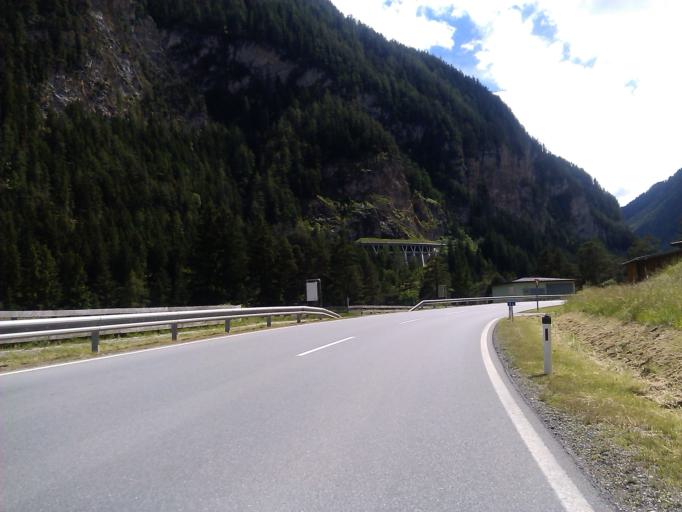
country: AT
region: Tyrol
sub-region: Politischer Bezirk Landeck
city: Pfunds
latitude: 46.9468
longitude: 10.5056
